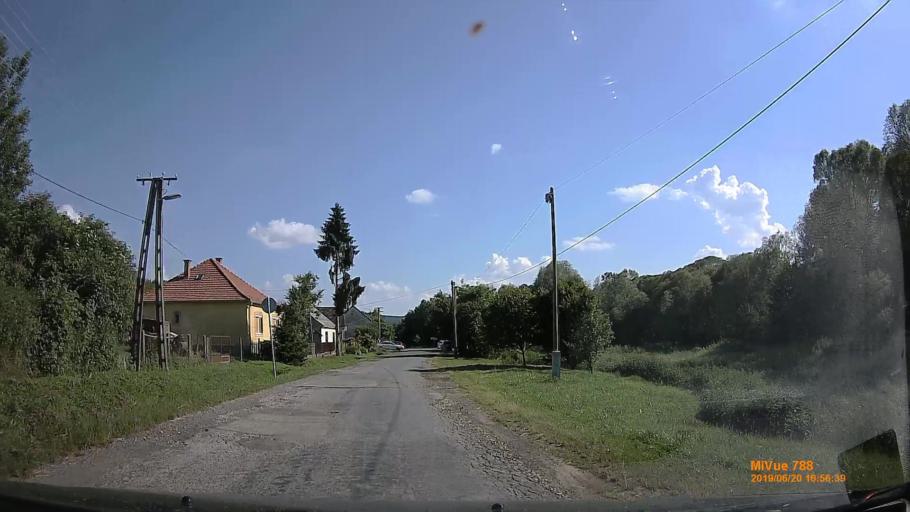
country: HU
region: Baranya
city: Buekkoesd
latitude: 46.1482
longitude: 18.0602
